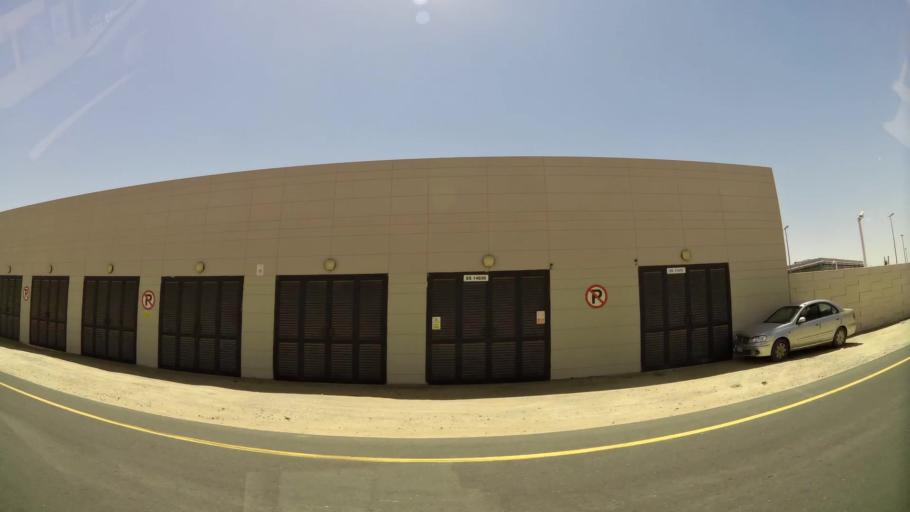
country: AE
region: Dubai
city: Dubai
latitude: 24.9750
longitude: 55.1942
